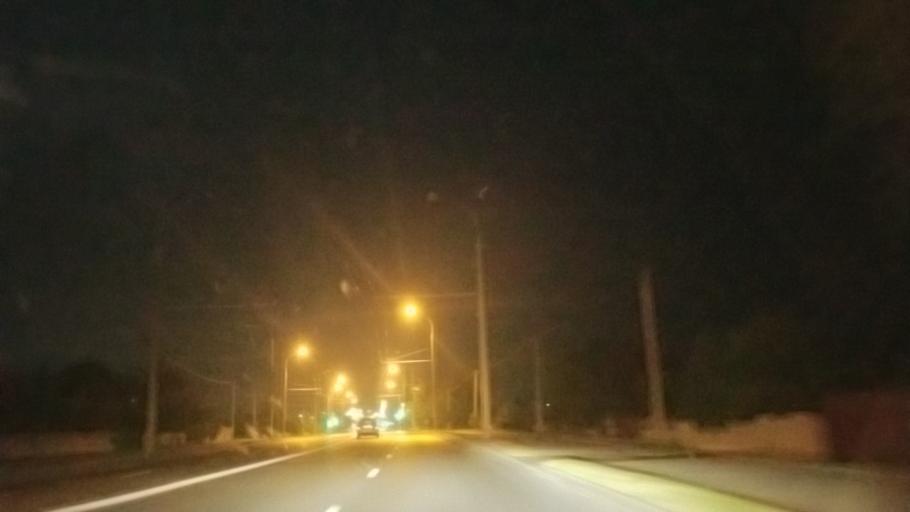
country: BY
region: Brest
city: Brest
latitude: 52.0731
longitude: 23.7646
